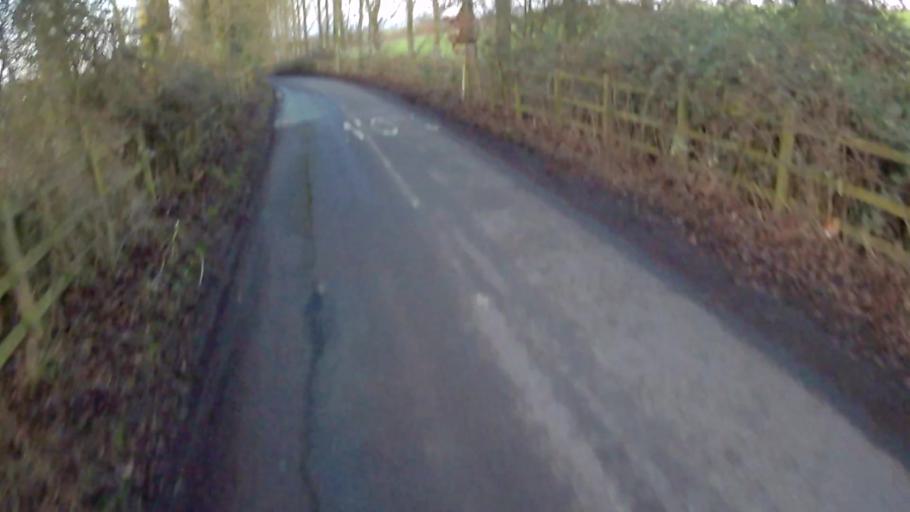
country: GB
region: England
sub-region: Hampshire
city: Overton
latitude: 51.2408
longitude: -1.2178
